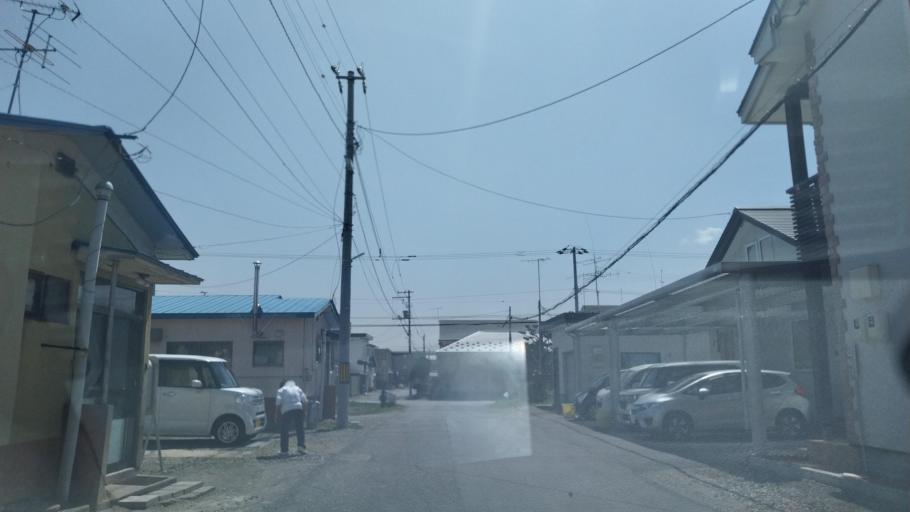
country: JP
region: Hokkaido
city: Obihiro
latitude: 42.9329
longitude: 143.1729
